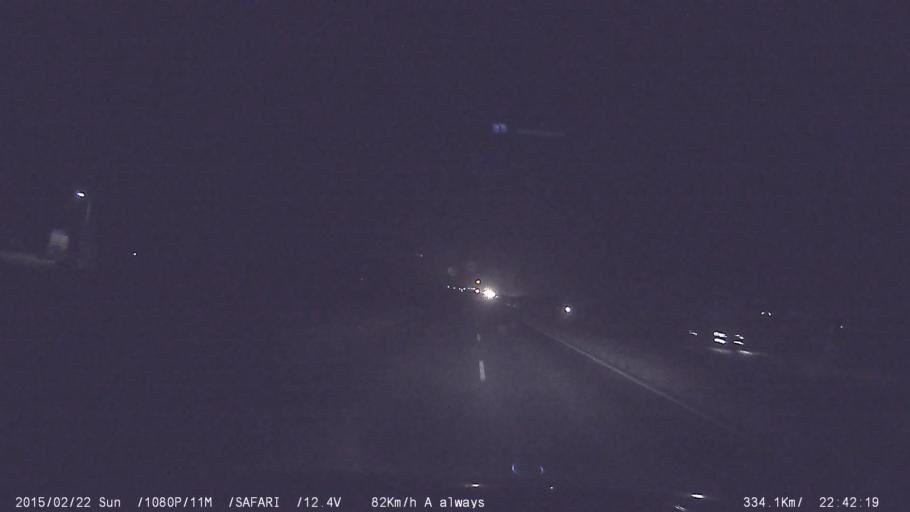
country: IN
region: Tamil Nadu
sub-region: Namakkal
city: Namakkal
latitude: 11.1877
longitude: 78.0807
